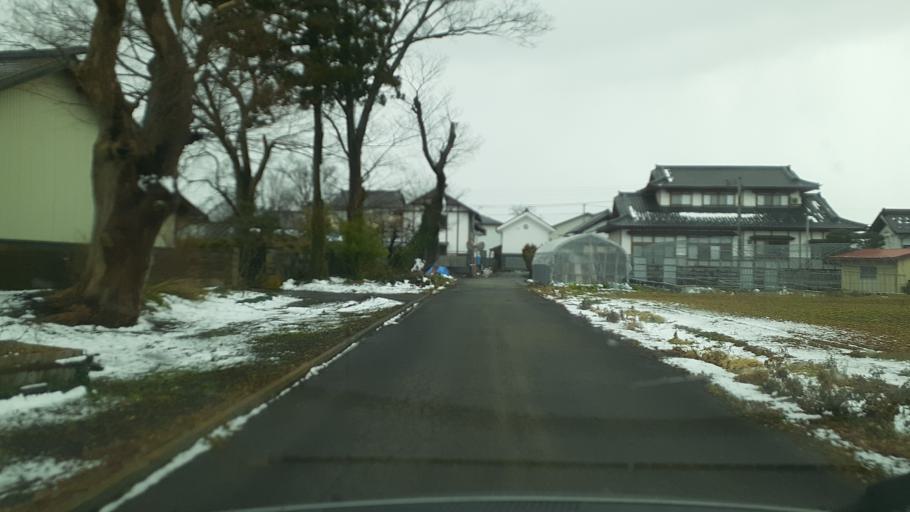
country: JP
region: Fukushima
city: Kitakata
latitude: 37.5603
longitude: 139.8878
